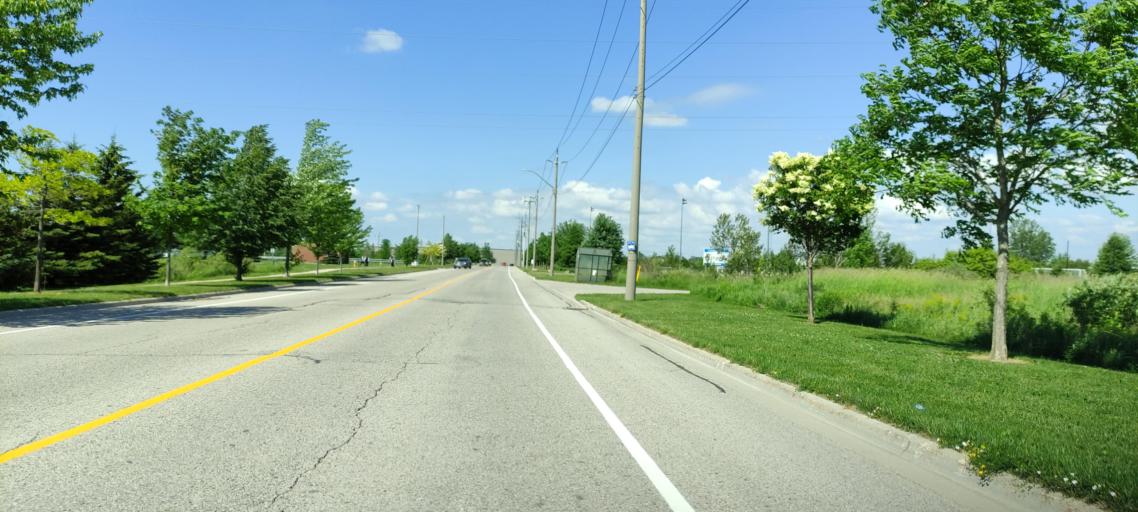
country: CA
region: Ontario
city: Stratford
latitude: 43.3467
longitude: -81.0095
